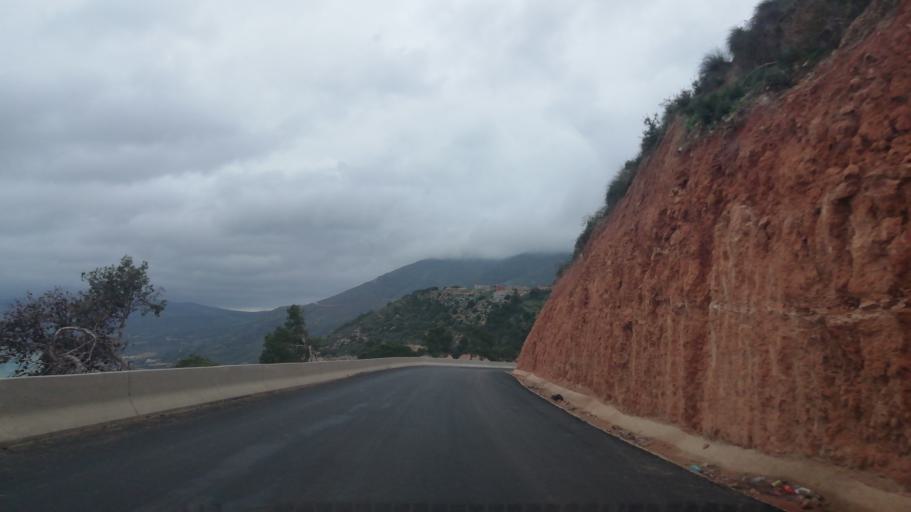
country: DZ
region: Oran
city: Bir el Djir
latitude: 35.7614
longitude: -0.5313
